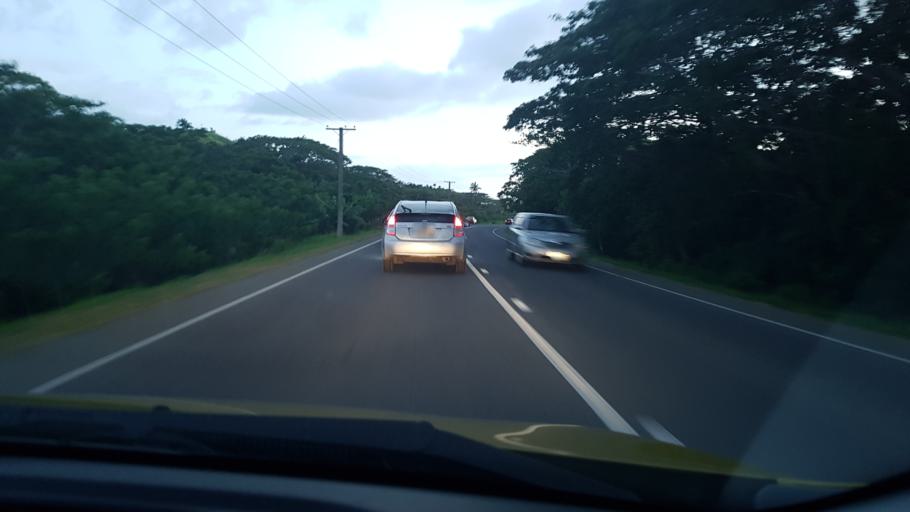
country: FJ
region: Western
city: Nadi
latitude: -18.1487
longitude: 177.5133
